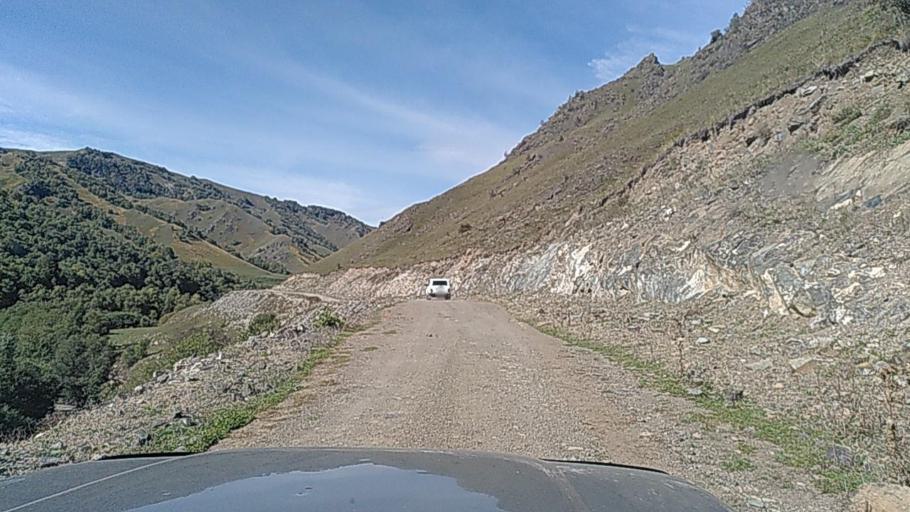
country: RU
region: Kabardino-Balkariya
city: Kamennomostskoye
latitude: 43.7189
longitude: 42.8876
